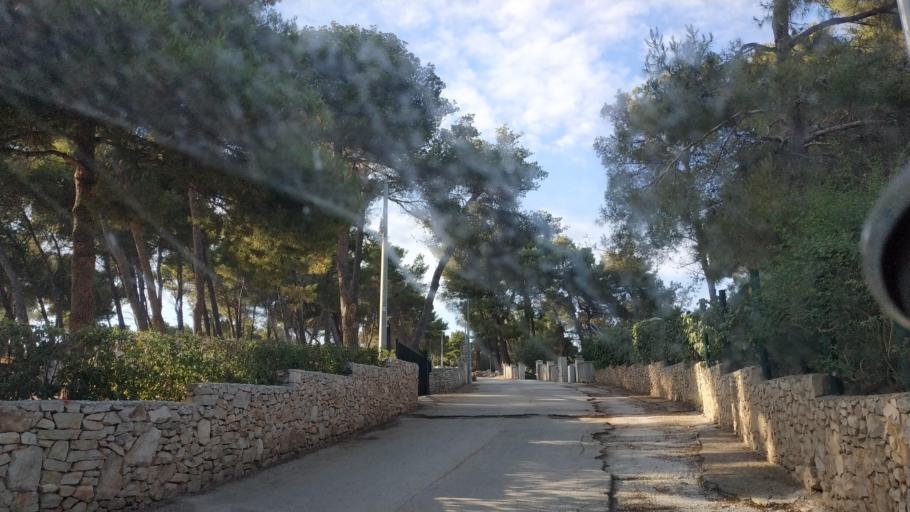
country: HR
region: Splitsko-Dalmatinska
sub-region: Grad Trogir
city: Trogir
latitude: 43.4820
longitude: 16.2446
